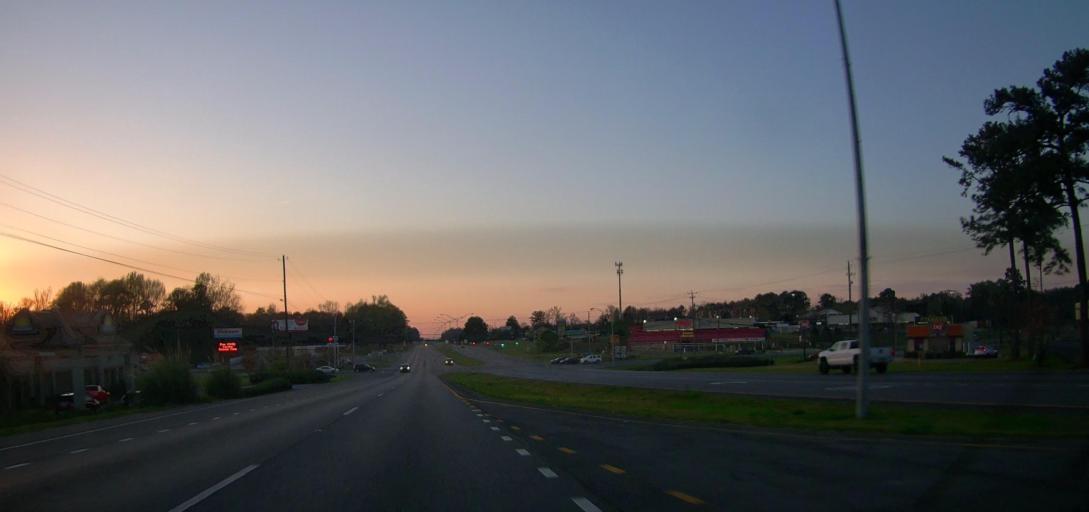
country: US
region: Alabama
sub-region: Tallapoosa County
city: Alexander City
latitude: 32.9328
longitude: -85.9705
